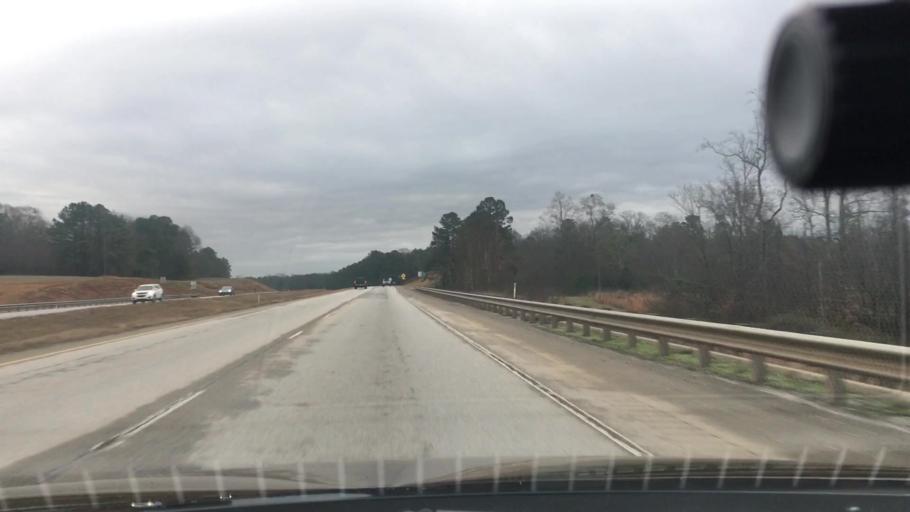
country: US
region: Georgia
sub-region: Henry County
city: Locust Grove
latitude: 33.2594
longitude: -84.1188
